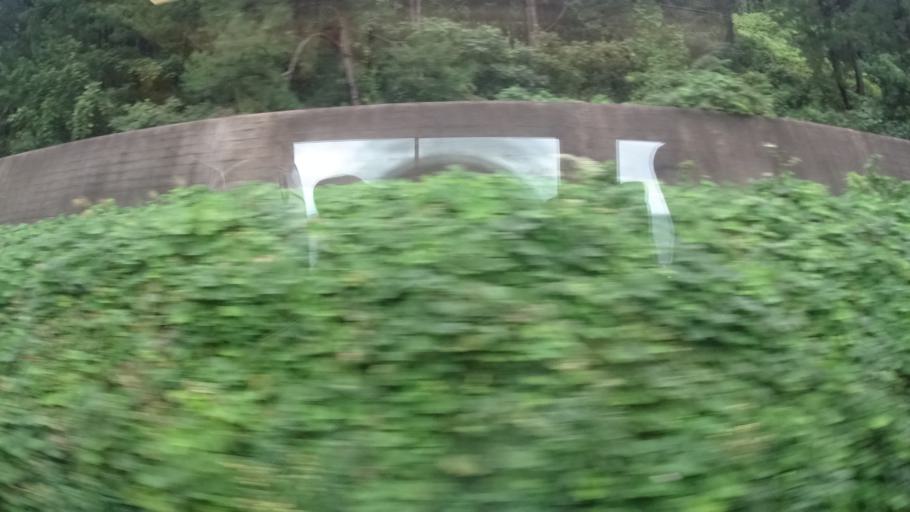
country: JP
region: Niigata
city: Murakami
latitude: 38.3813
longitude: 139.4609
